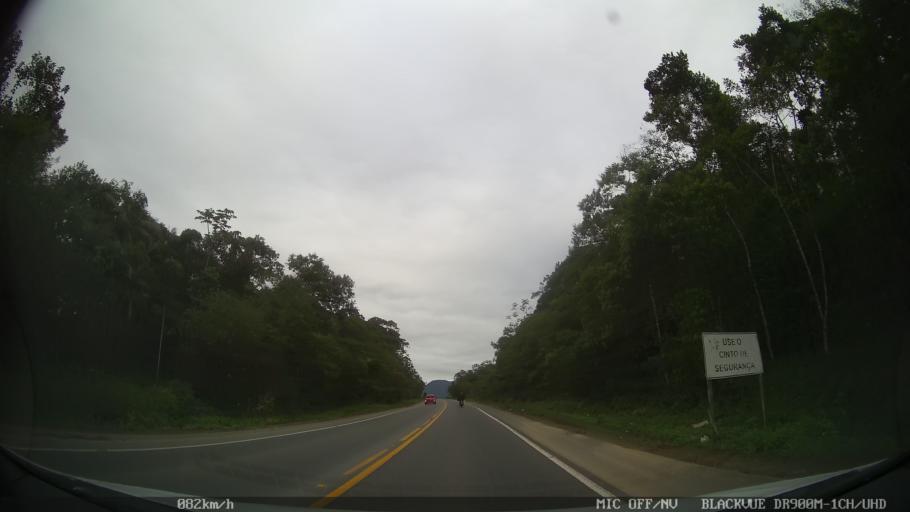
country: BR
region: Santa Catarina
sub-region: Joinville
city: Joinville
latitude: -26.2630
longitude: -48.9161
